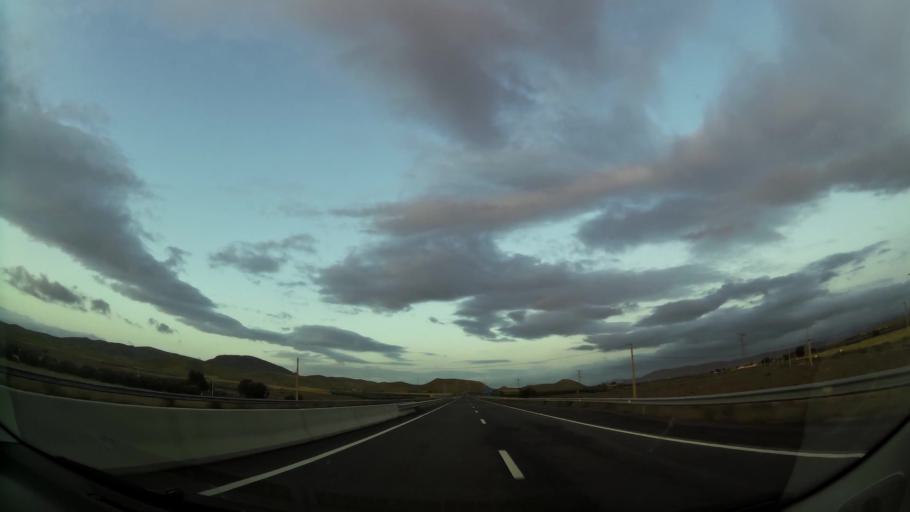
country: MA
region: Oriental
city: El Aioun
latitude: 34.5938
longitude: -2.6932
